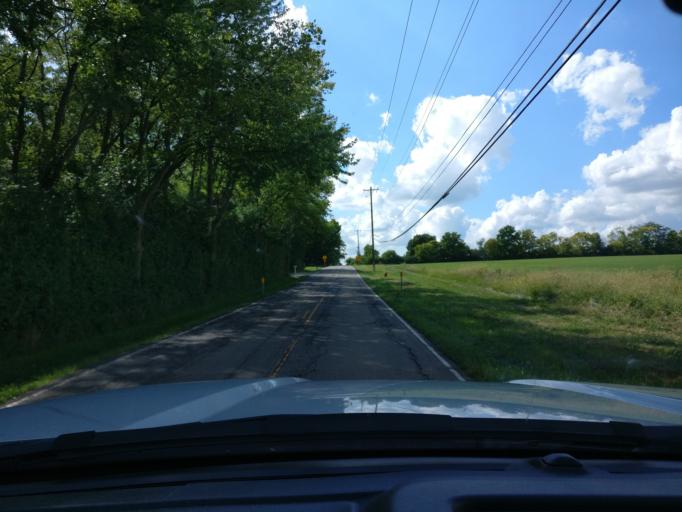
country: US
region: Ohio
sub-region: Warren County
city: Springboro
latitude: 39.5072
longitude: -84.2355
